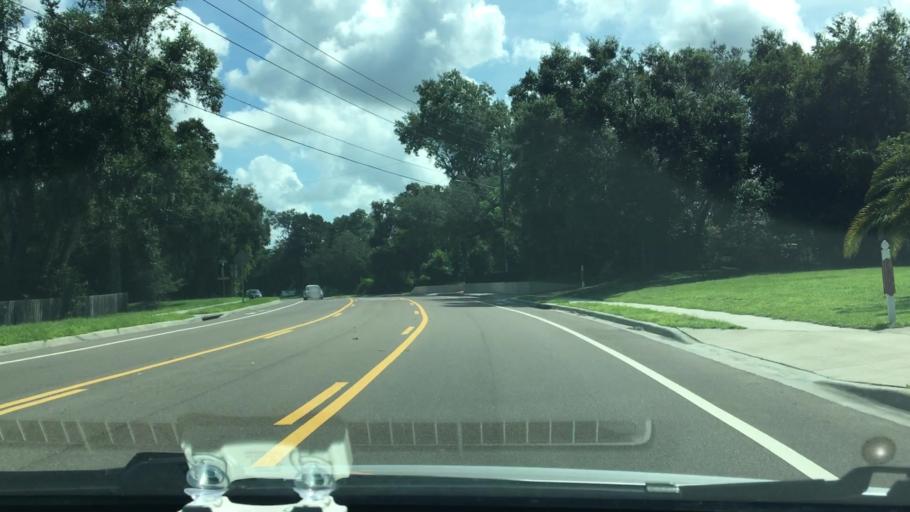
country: US
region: Florida
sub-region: Volusia County
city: Deltona
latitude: 28.8852
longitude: -81.2217
